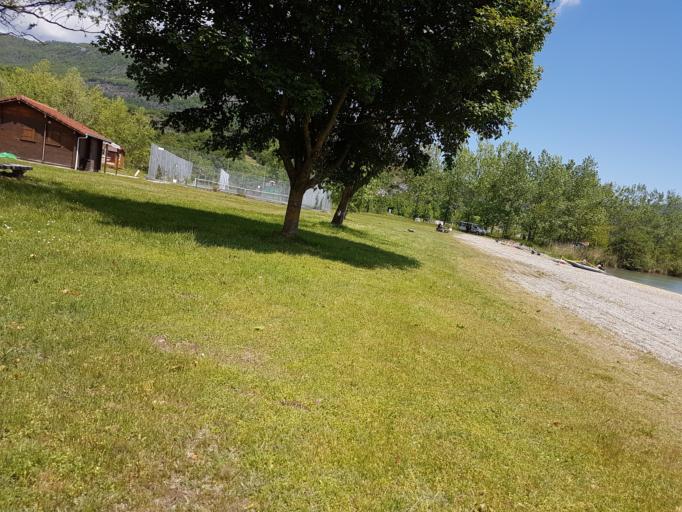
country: FR
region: Rhone-Alpes
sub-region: Departement de la Savoie
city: Saint-Genix-sur-Guiers
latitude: 45.6374
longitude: 5.6425
